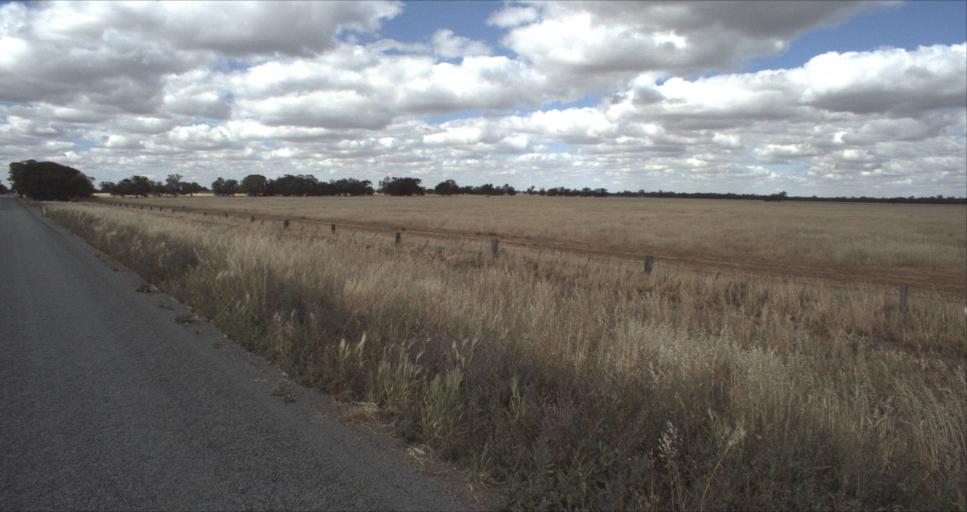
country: AU
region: New South Wales
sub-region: Leeton
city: Leeton
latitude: -34.6948
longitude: 146.3430
